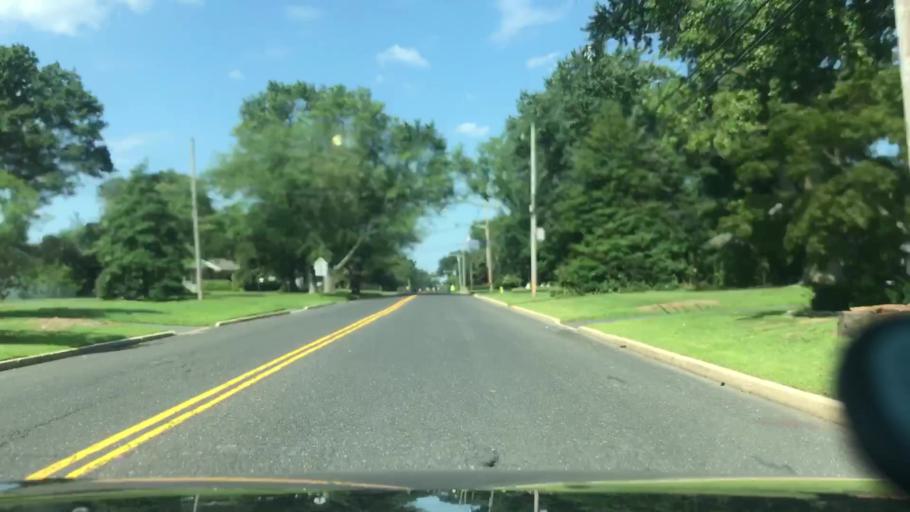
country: US
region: New Jersey
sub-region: Monmouth County
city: Oceanport
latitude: 40.3208
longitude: -74.0009
